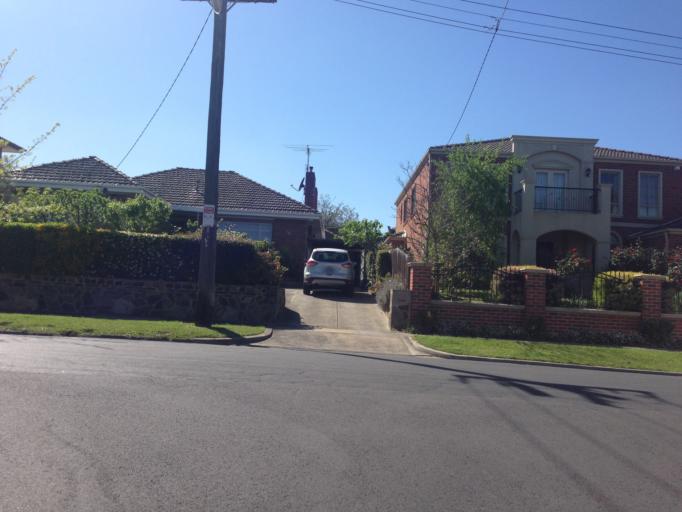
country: AU
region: Victoria
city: Balwyn
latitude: -37.8036
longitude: 145.0689
